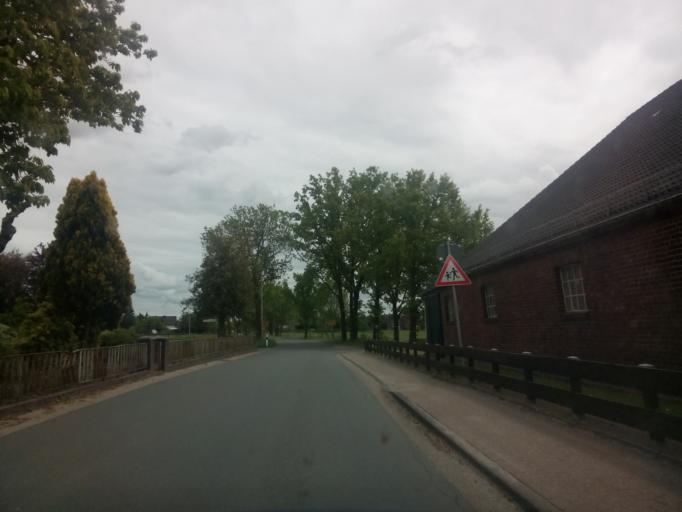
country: DE
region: Lower Saxony
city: Lemwerder
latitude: 53.1768
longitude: 8.5571
